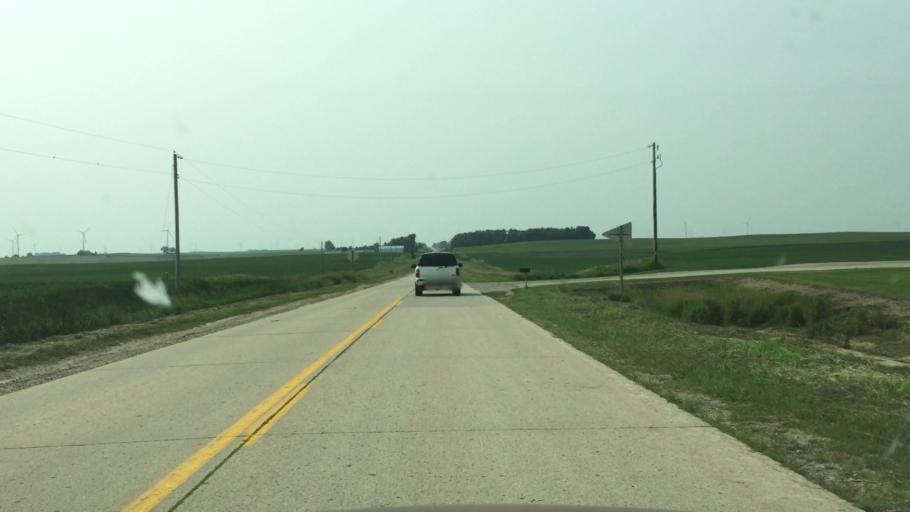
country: US
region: Iowa
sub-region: Dickinson County
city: Lake Park
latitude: 43.4288
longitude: -95.2891
